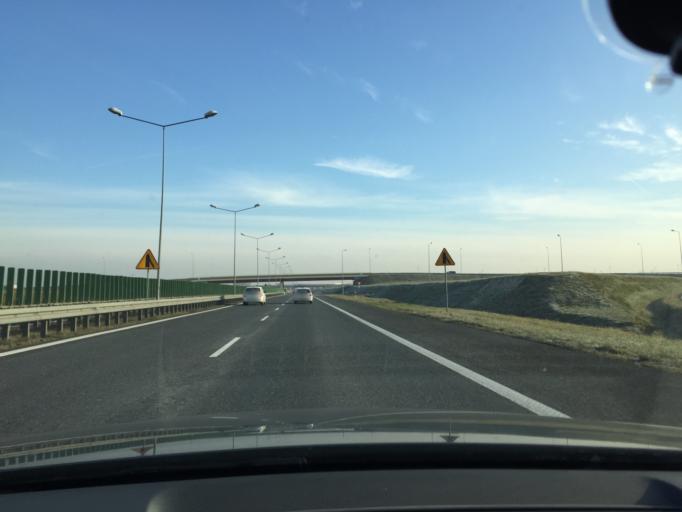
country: PL
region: Silesian Voivodeship
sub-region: Powiat gliwicki
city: Zernica
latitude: 50.2604
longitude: 18.6469
